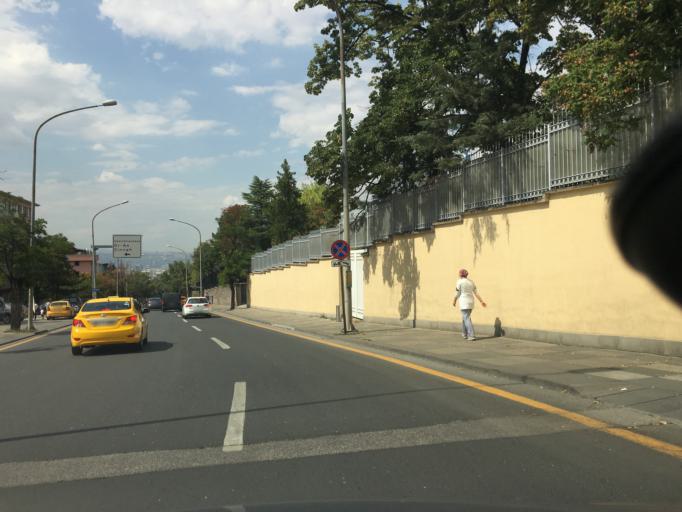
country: TR
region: Ankara
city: Cankaya
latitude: 39.8968
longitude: 32.8618
